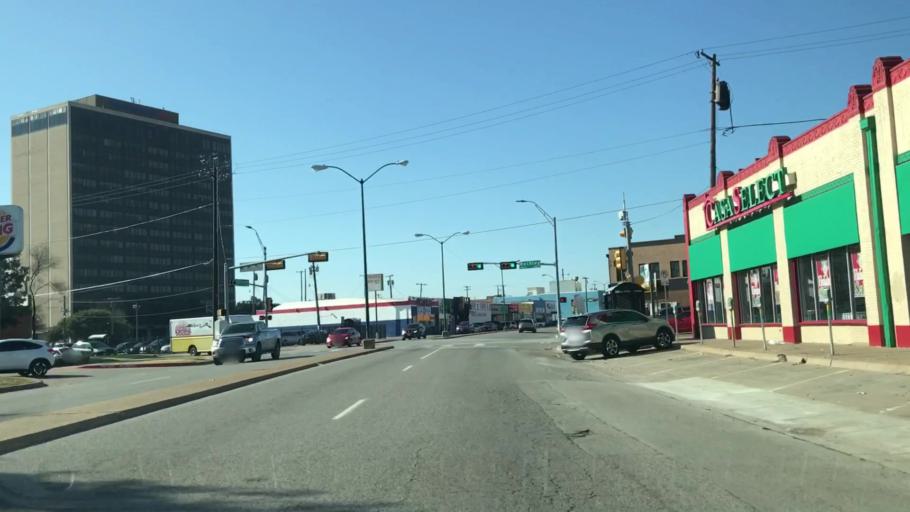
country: US
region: Texas
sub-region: Dallas County
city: Dallas
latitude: 32.7438
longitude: -96.8223
